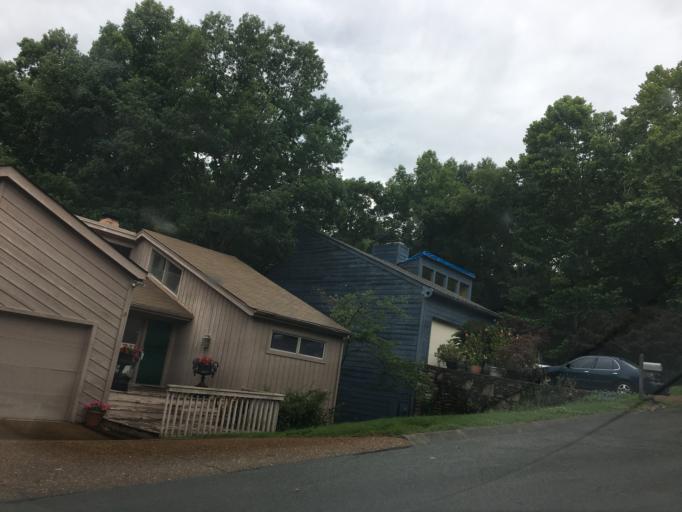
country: US
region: Tennessee
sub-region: Davidson County
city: Belle Meade
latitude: 36.0728
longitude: -86.8987
